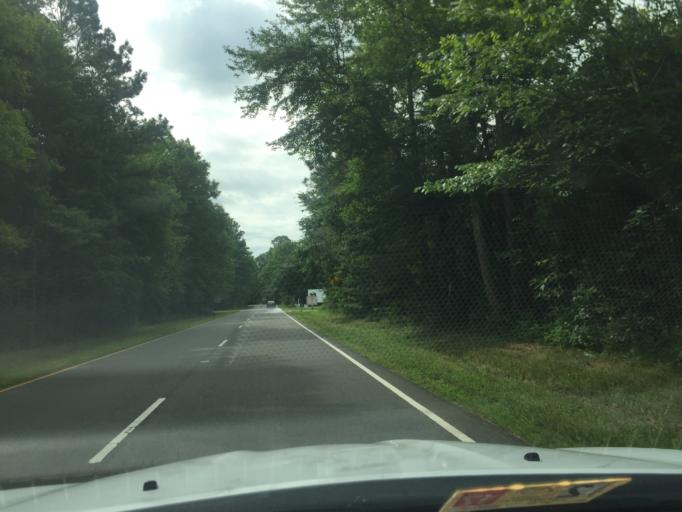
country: US
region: Virginia
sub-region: Charles City County
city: Charles City
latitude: 37.4523
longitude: -77.0787
